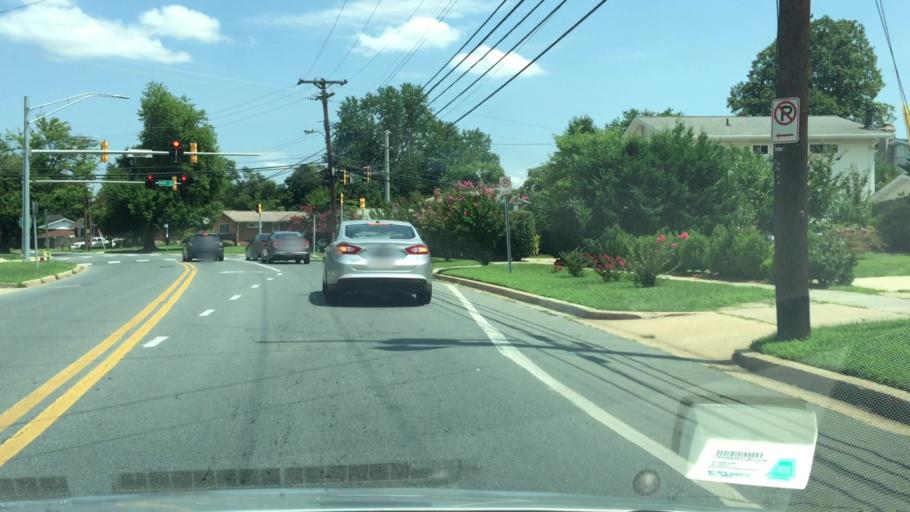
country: US
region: Maryland
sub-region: Montgomery County
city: Aspen Hill
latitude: 39.0712
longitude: -77.0996
